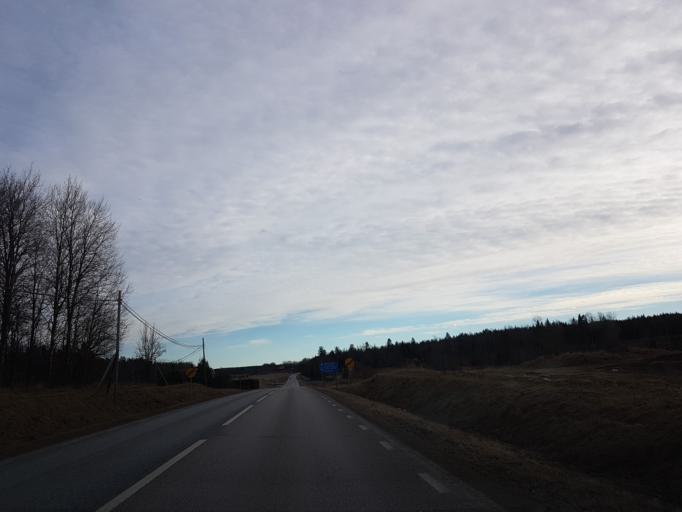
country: SE
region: Stockholm
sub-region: Vallentuna Kommun
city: Vallentuna
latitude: 59.6658
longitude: 18.0479
